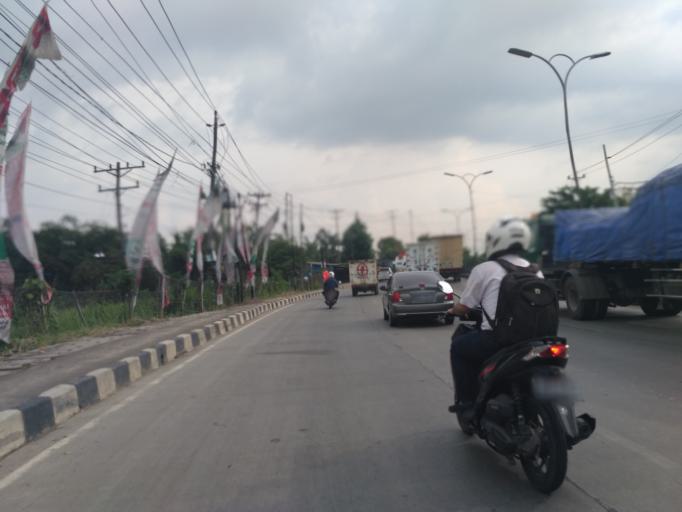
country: ID
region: Central Java
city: Semarang
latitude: -6.9848
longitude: 110.3490
